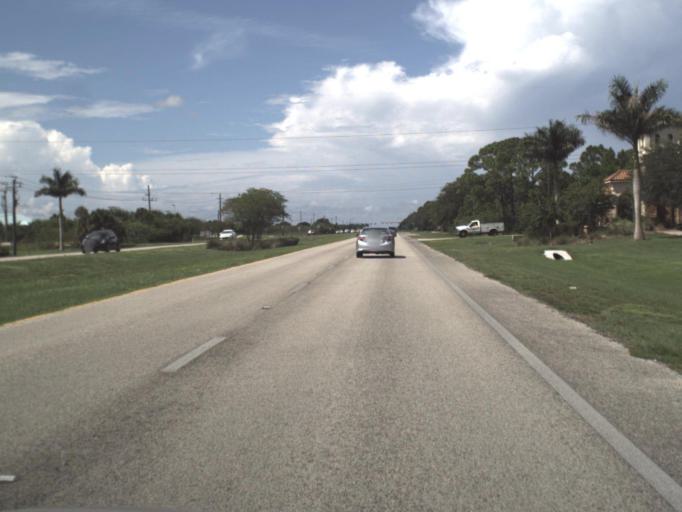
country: US
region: Florida
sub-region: Sarasota County
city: Plantation
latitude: 27.0498
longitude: -82.3505
